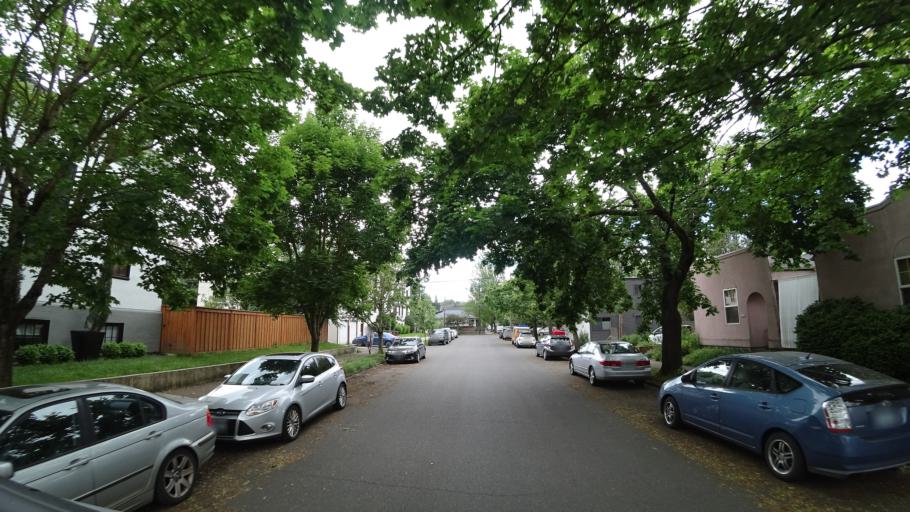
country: US
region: Oregon
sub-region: Multnomah County
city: Portland
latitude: 45.5086
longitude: -122.6528
